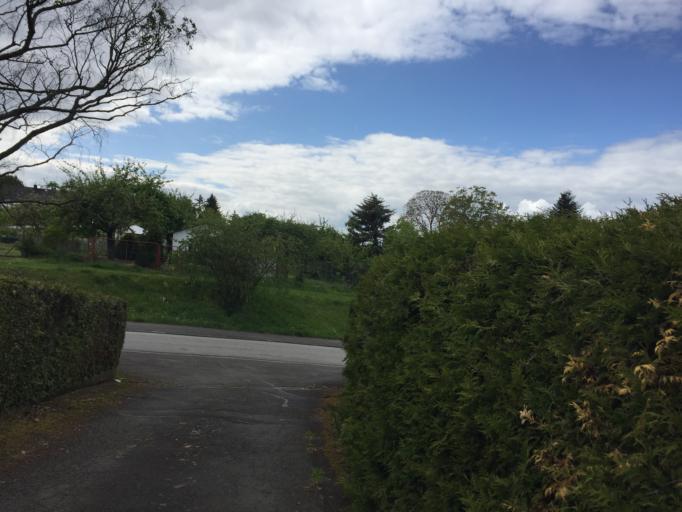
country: DE
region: Hesse
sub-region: Regierungsbezirk Giessen
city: Reiskirchen
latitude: 50.5759
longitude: 8.8186
